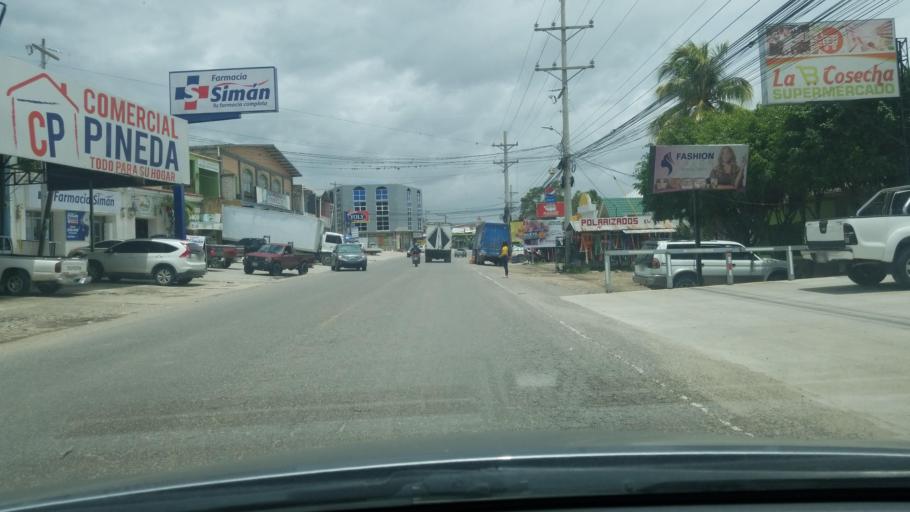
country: HN
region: Copan
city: Cucuyagua
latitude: 14.6534
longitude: -88.8756
